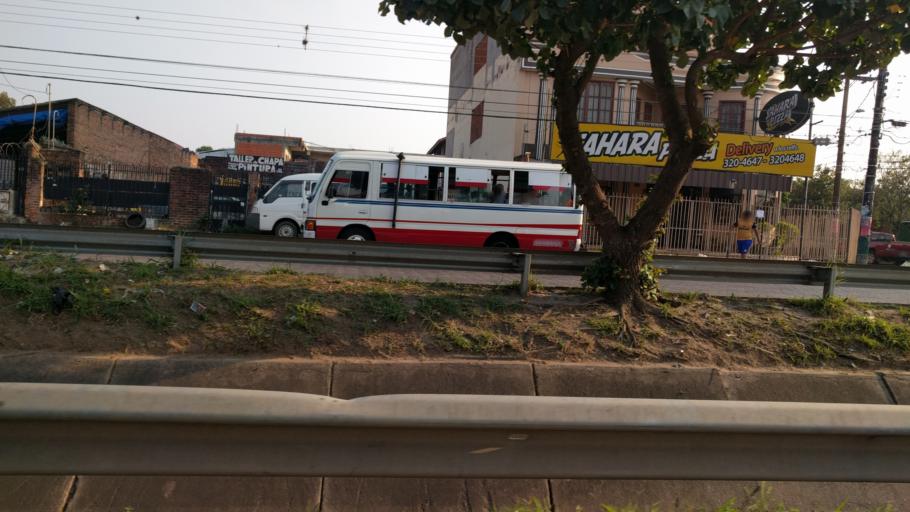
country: BO
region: Santa Cruz
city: Santa Cruz de la Sierra
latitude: -17.7964
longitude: -63.2113
